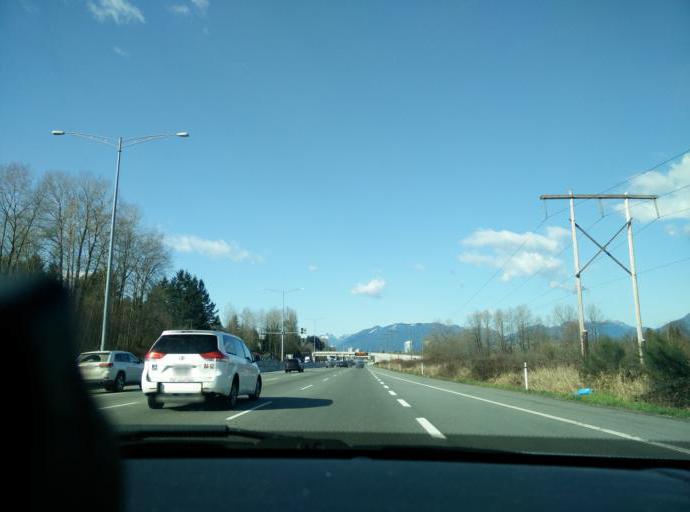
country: CA
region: British Columbia
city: Burnaby
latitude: 49.2462
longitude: -122.9699
